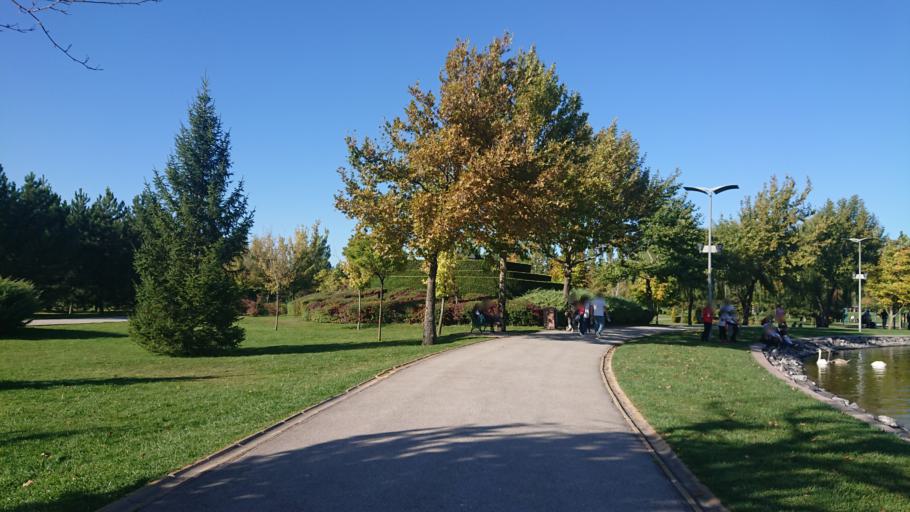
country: TR
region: Eskisehir
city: Eskisehir
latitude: 39.7629
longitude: 30.4721
